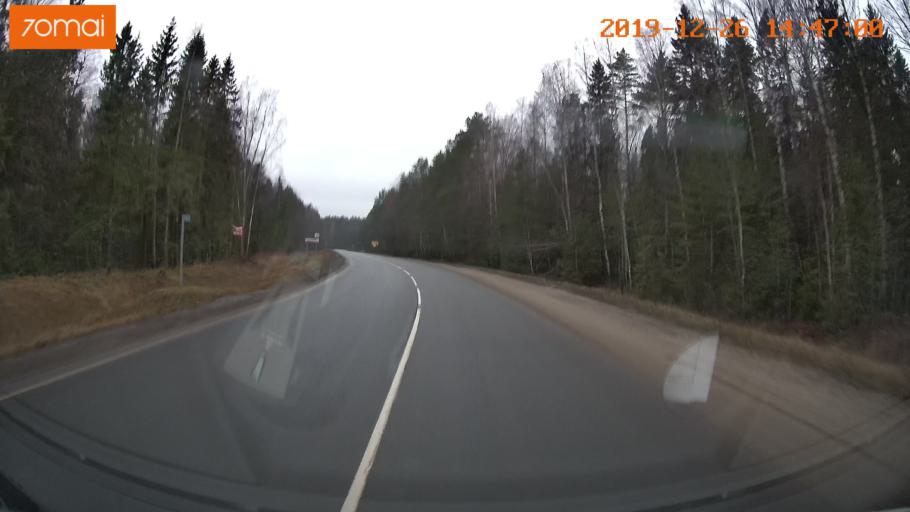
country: RU
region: Jaroslavl
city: Poshekhon'ye
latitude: 58.3413
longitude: 39.0081
